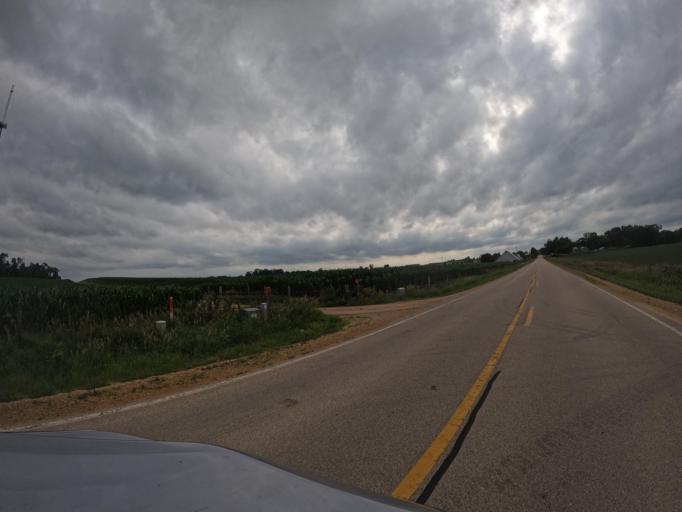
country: US
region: Iowa
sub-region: Clinton County
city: De Witt
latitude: 41.8005
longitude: -90.5341
